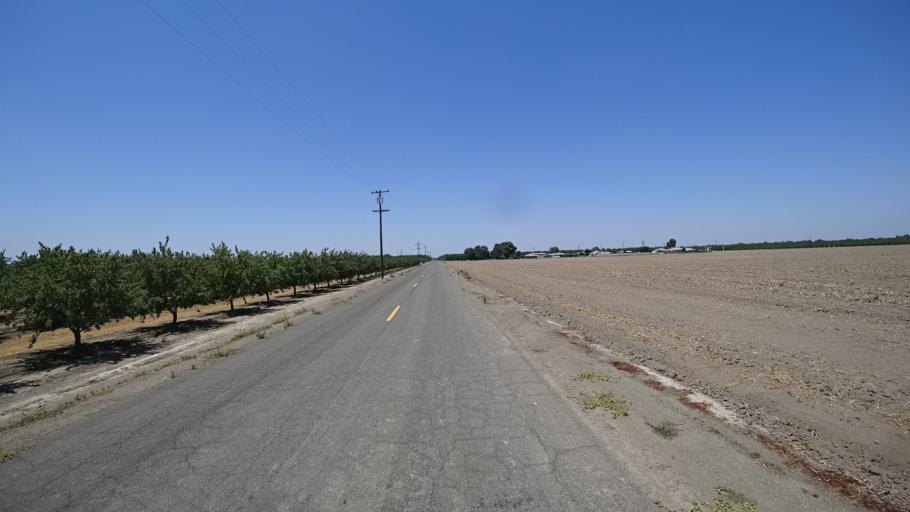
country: US
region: California
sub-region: Fresno County
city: Laton
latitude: 36.3865
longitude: -119.7414
